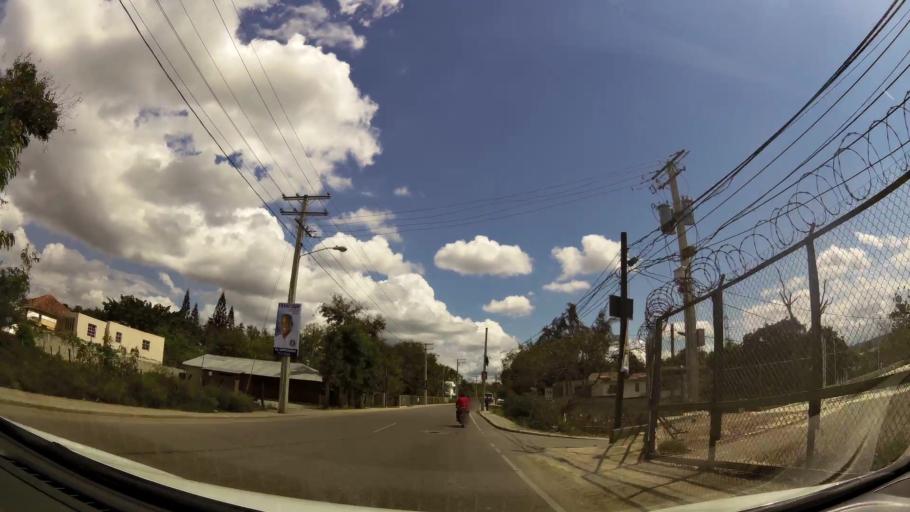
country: DO
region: Santiago
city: Santiago de los Caballeros
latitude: 19.4170
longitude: -70.6784
